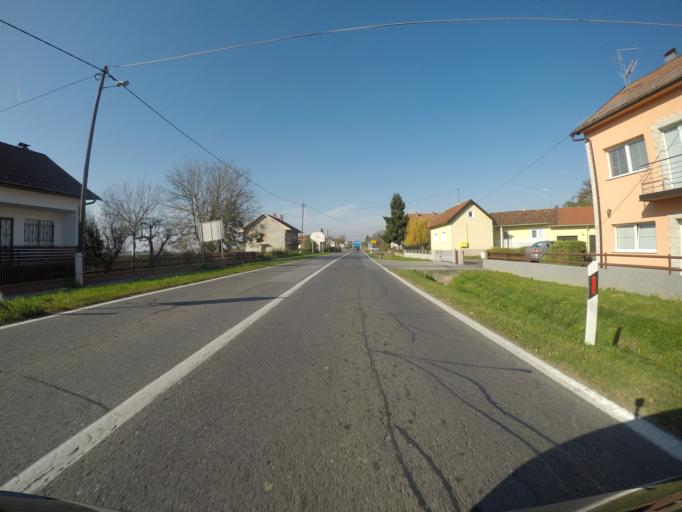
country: HR
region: Bjelovarsko-Bilogorska
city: Predavac
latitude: 45.9232
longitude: 16.7885
